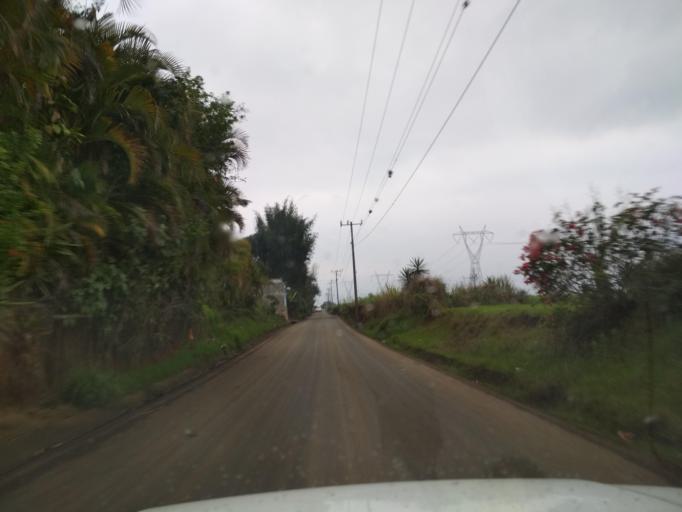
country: MX
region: Veracruz
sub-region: Cordoba
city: Veinte de Noviembre
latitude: 18.8684
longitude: -96.9633
